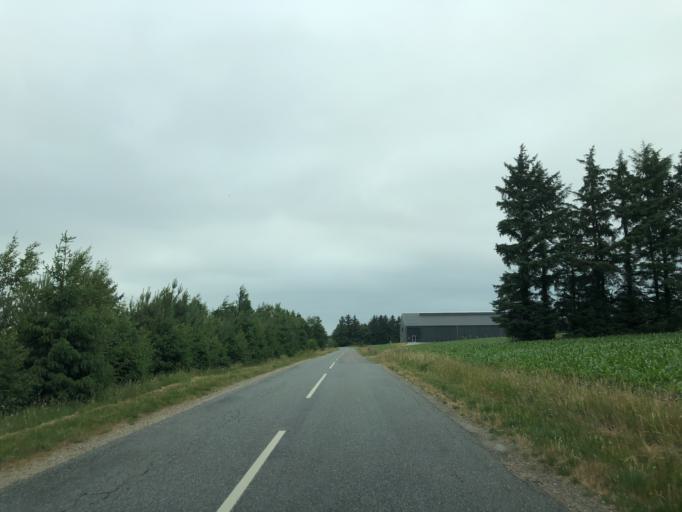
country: DK
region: Central Jutland
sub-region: Ringkobing-Skjern Kommune
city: Videbaek
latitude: 56.2021
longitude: 8.5706
